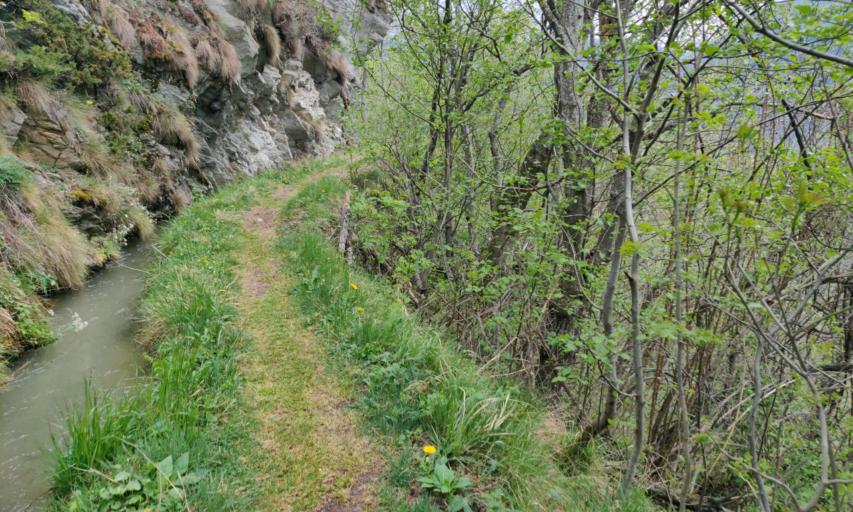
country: CH
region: Valais
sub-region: Visp District
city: Baltschieder
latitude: 46.3163
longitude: 7.8840
